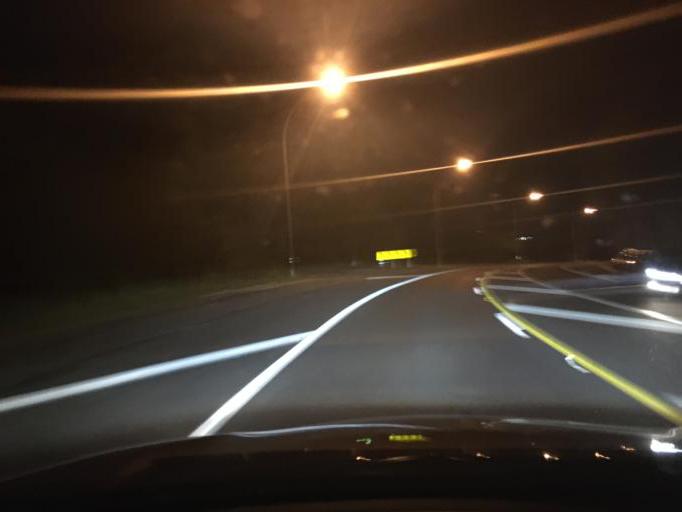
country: NZ
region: Waikato
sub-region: Hamilton City
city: Hamilton
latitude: -37.8264
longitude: 175.2962
